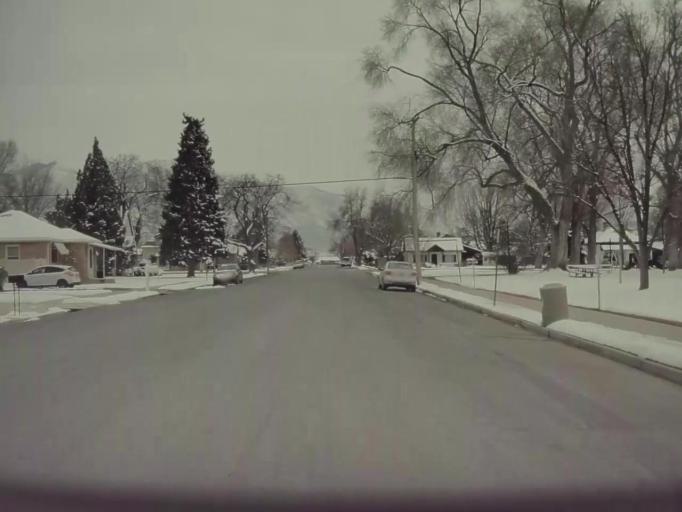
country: US
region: Utah
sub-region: Utah County
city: Spanish Fork
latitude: 40.1091
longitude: -111.6531
